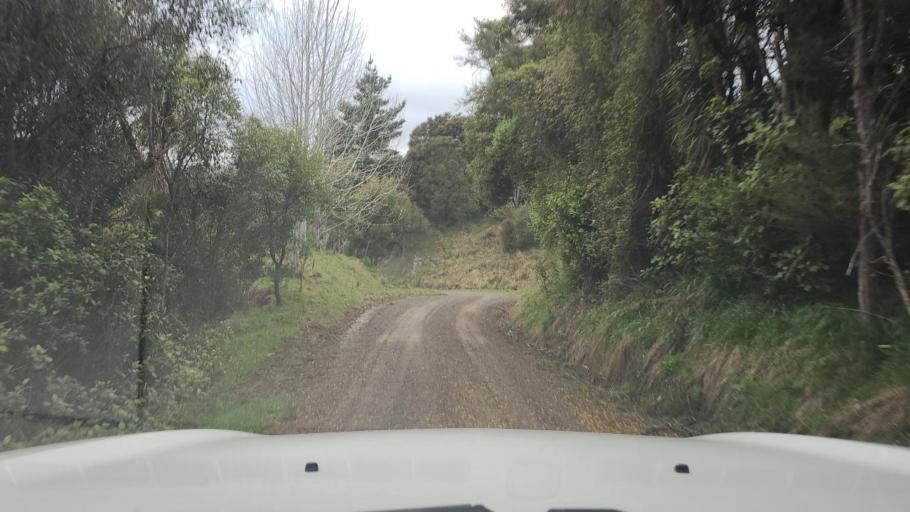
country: NZ
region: Wellington
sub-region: Masterton District
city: Masterton
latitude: -41.1635
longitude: 175.6879
